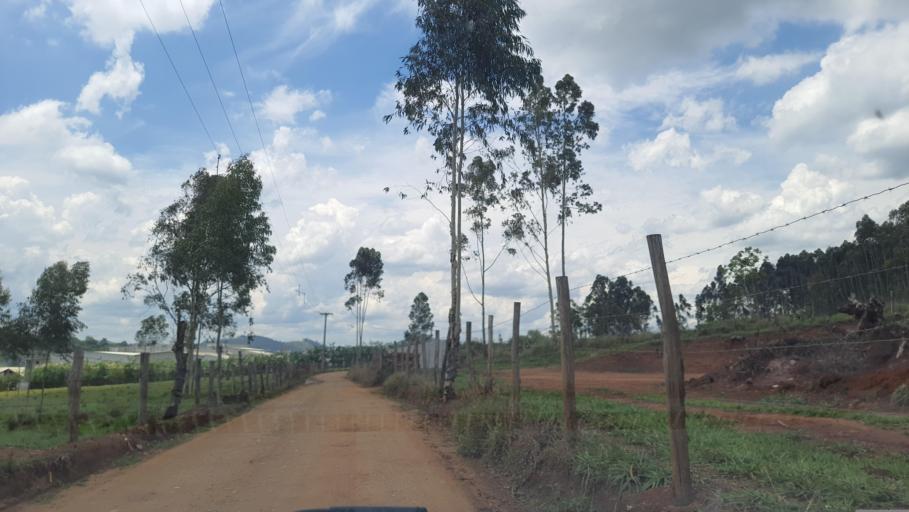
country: BR
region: Sao Paulo
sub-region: Bom Jesus Dos Perdoes
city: Bom Jesus dos Perdoes
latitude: -23.1523
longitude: -46.4627
